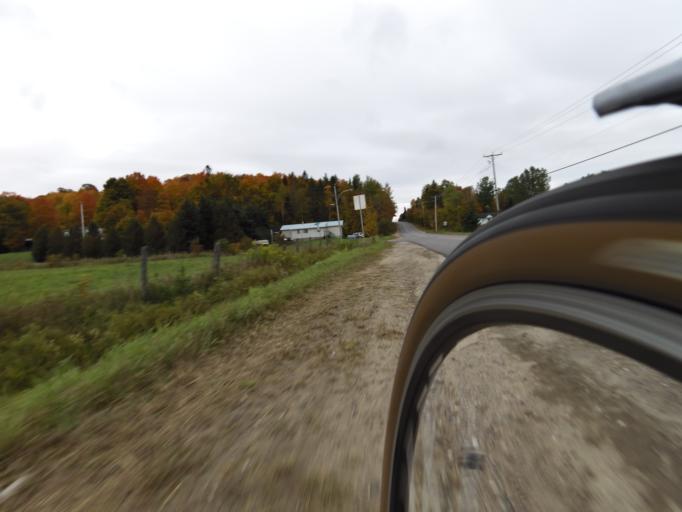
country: CA
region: Quebec
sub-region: Outaouais
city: Wakefield
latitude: 45.6534
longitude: -76.0163
